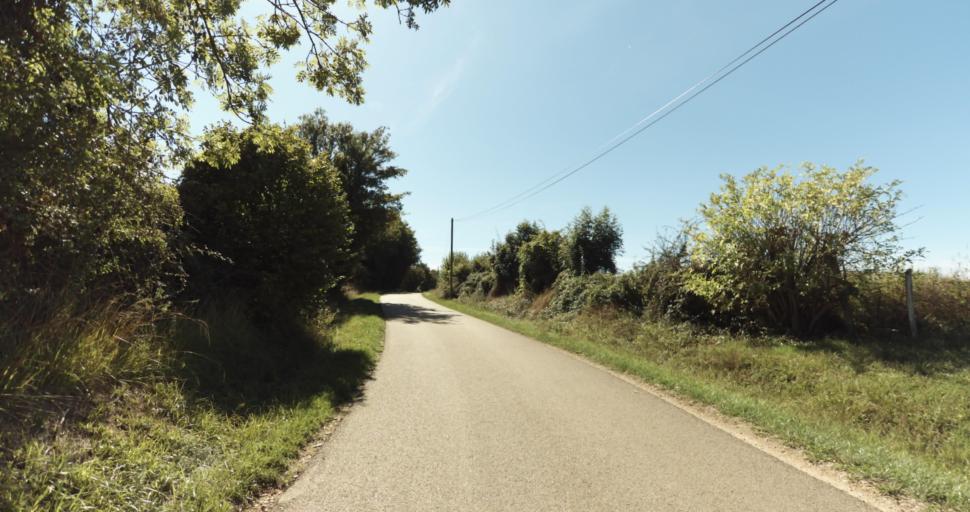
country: FR
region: Lower Normandy
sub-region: Departement de l'Orne
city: Gace
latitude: 48.7889
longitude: 0.2849
